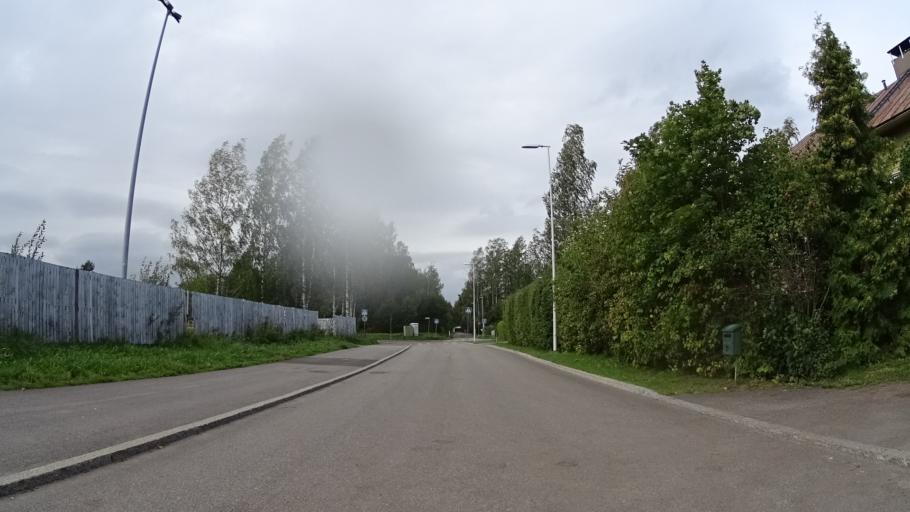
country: FI
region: Uusimaa
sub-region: Helsinki
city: Vantaa
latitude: 60.2950
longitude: 25.0063
